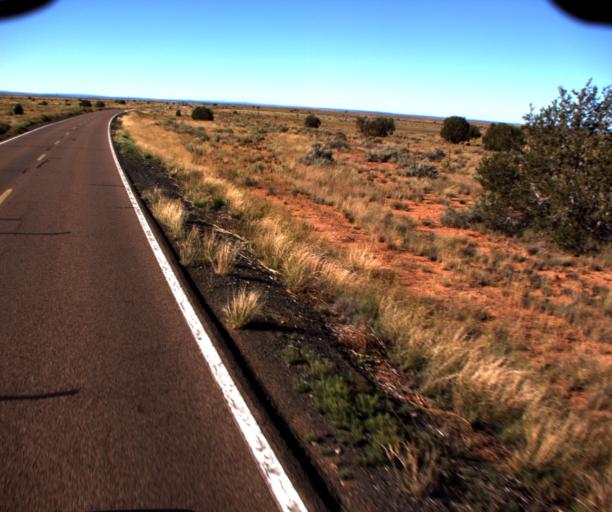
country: US
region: Arizona
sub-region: Navajo County
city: Heber-Overgaard
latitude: 34.6313
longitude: -110.3617
